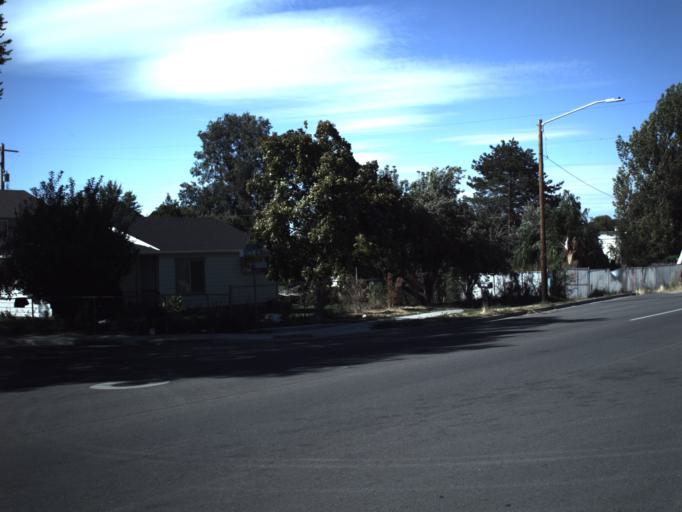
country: US
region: Utah
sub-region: Davis County
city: North Salt Lake
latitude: 40.7992
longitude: -111.9391
